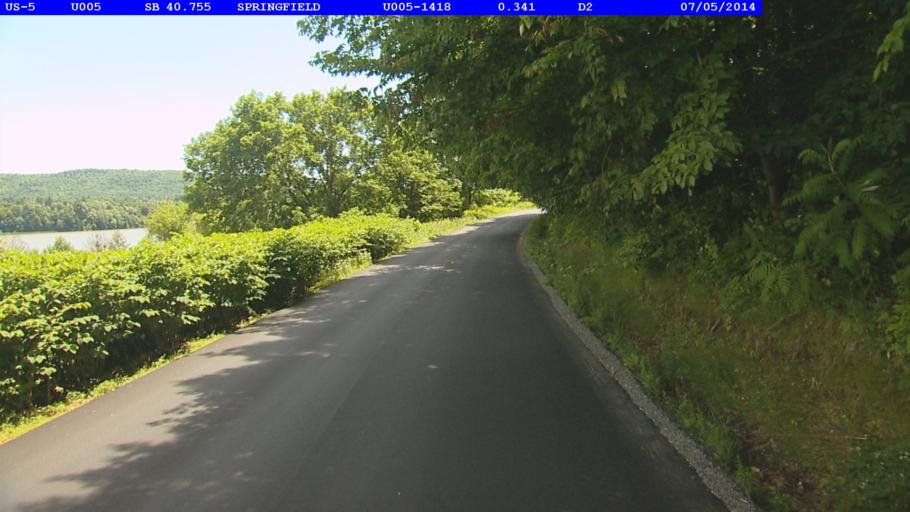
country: US
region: New Hampshire
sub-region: Sullivan County
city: Charlestown
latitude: 43.2381
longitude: -72.4384
